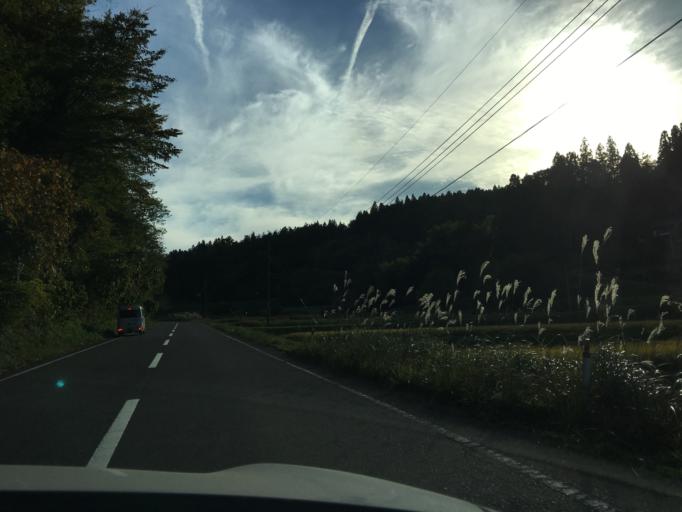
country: JP
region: Fukushima
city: Ishikawa
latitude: 37.2158
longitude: 140.5987
